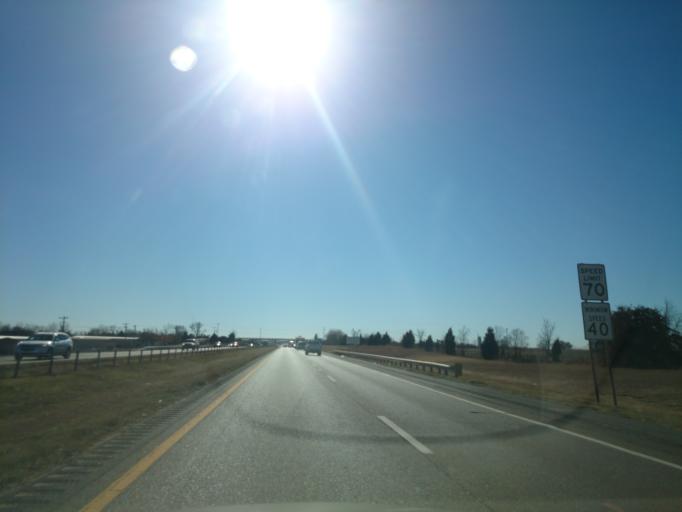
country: US
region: Oklahoma
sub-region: Oklahoma County
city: Edmond
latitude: 35.7145
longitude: -97.4164
